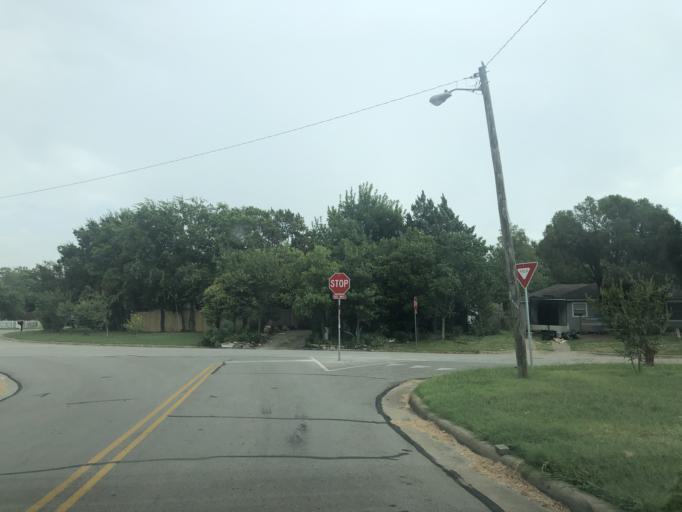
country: US
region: Texas
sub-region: Dallas County
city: Grand Prairie
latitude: 32.7421
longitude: -97.0114
